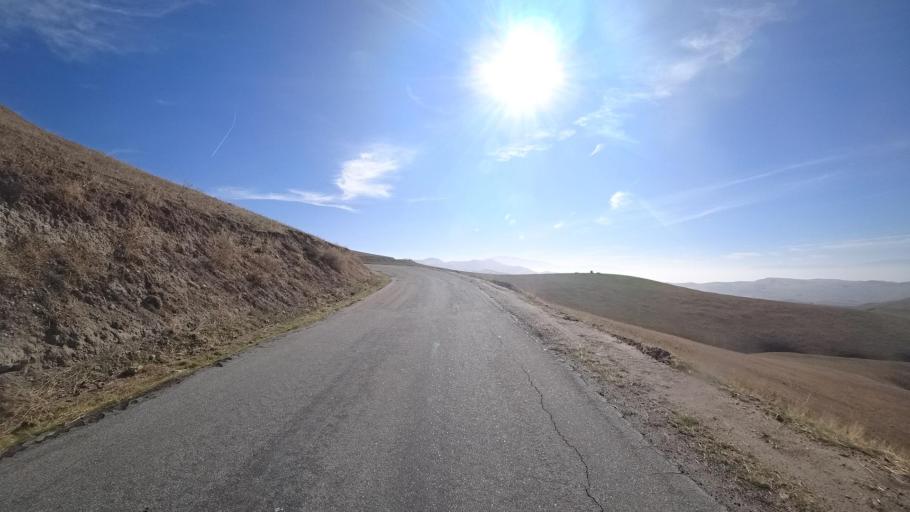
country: US
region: California
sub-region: Kern County
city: Arvin
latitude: 35.4132
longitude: -118.7531
